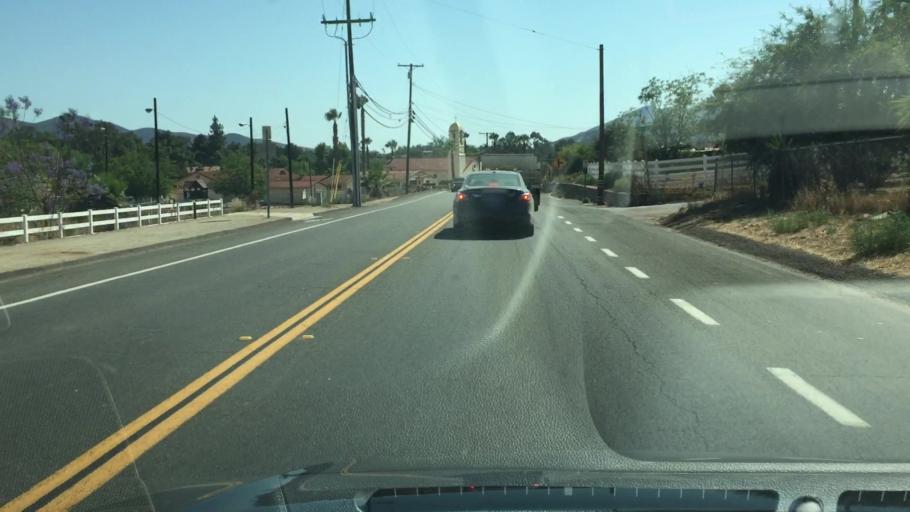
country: US
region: California
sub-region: San Diego County
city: Jamul
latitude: 32.7266
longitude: -116.8675
